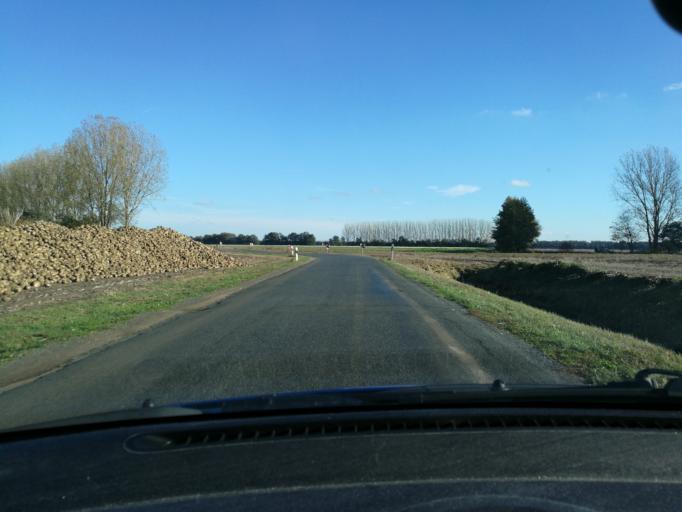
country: DE
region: Mecklenburg-Vorpommern
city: Neu Kaliss
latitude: 53.1475
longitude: 11.3019
